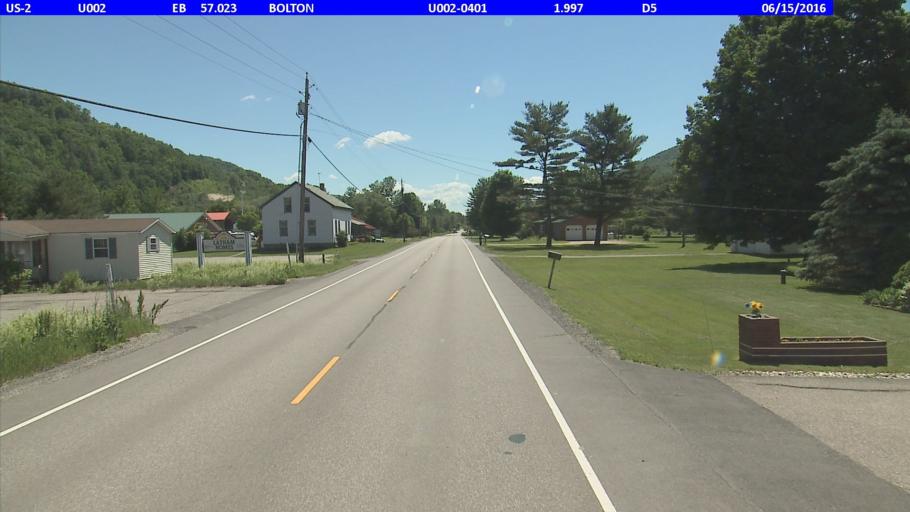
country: US
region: Vermont
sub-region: Washington County
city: Waterbury
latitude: 44.3762
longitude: -72.8947
